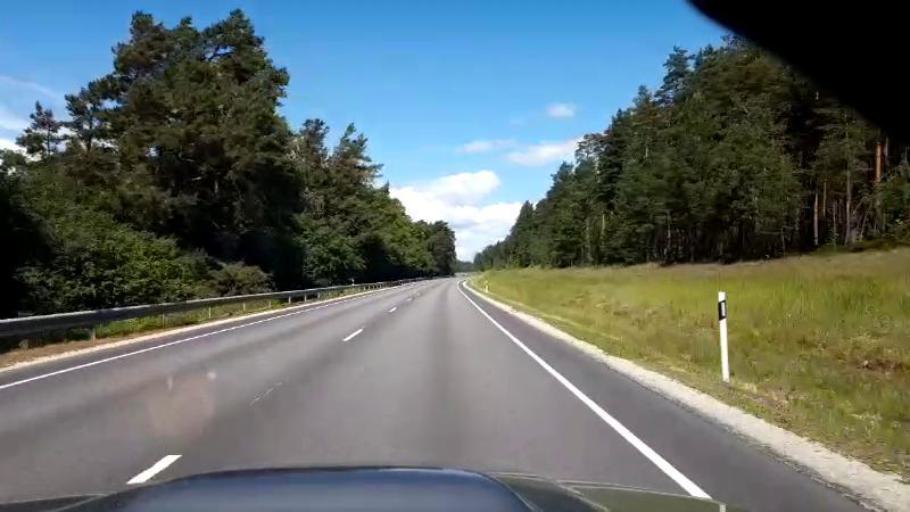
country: EE
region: Paernumaa
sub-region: Paernu linn
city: Parnu
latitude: 58.1698
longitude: 24.4955
